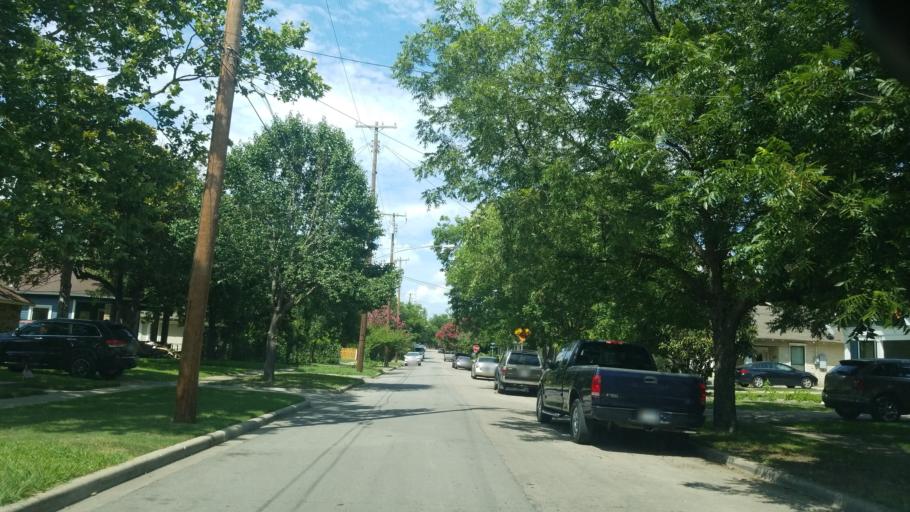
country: US
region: Texas
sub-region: Dallas County
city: Dallas
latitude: 32.8002
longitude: -96.7738
